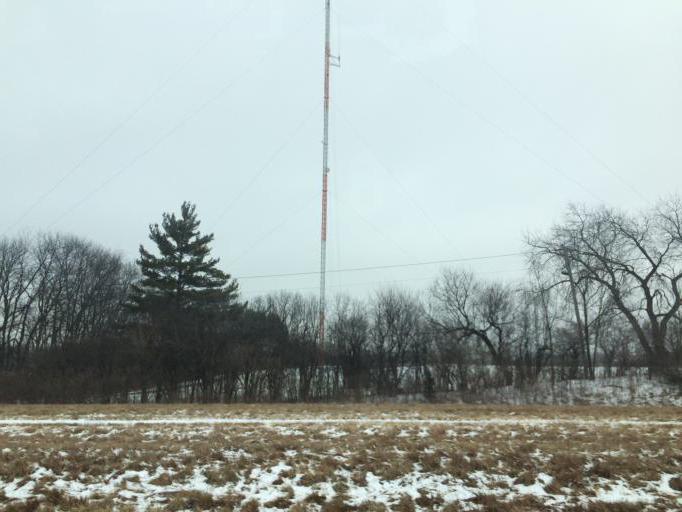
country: US
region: Illinois
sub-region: McHenry County
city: Woodstock
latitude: 42.3123
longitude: -88.4728
